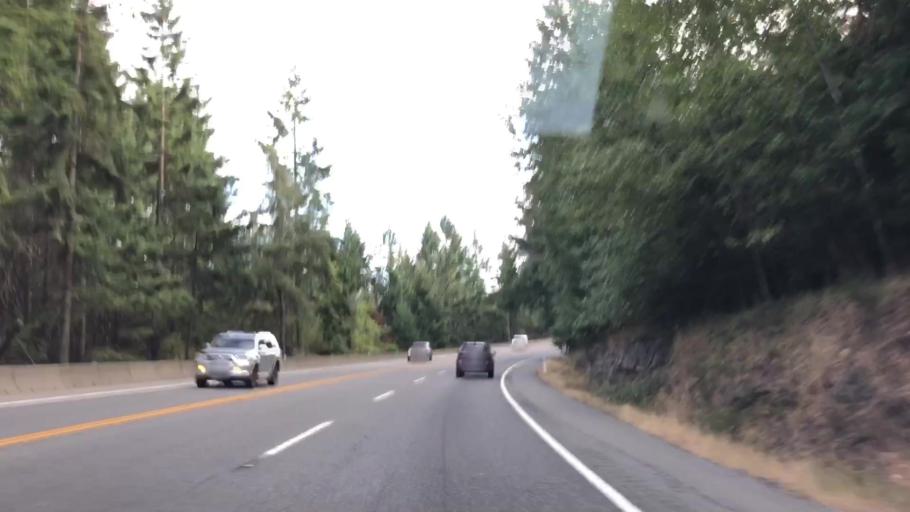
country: CA
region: British Columbia
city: Langford
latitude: 48.5744
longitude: -123.5269
